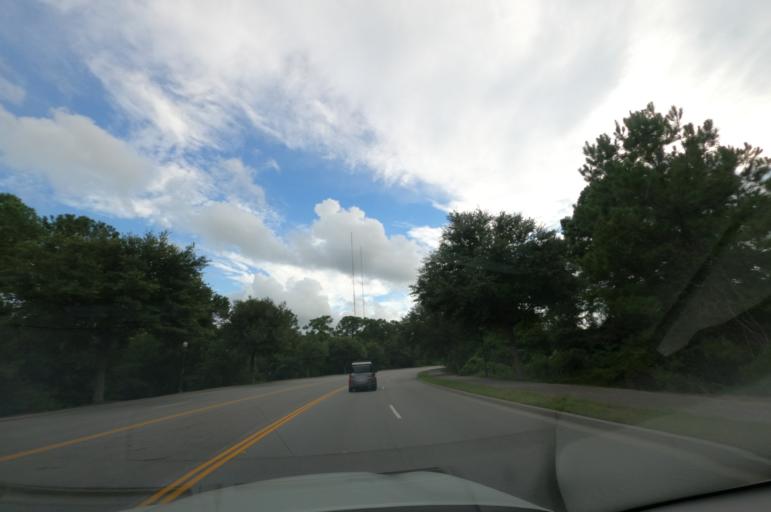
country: US
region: South Carolina
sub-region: Charleston County
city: Mount Pleasant
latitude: 32.8222
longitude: -79.8359
